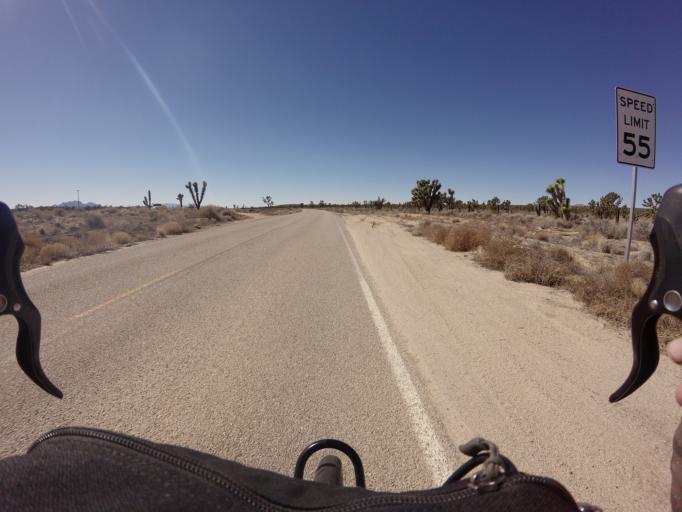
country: US
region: Nevada
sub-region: Clark County
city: Sandy Valley
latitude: 35.2335
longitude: -115.5051
